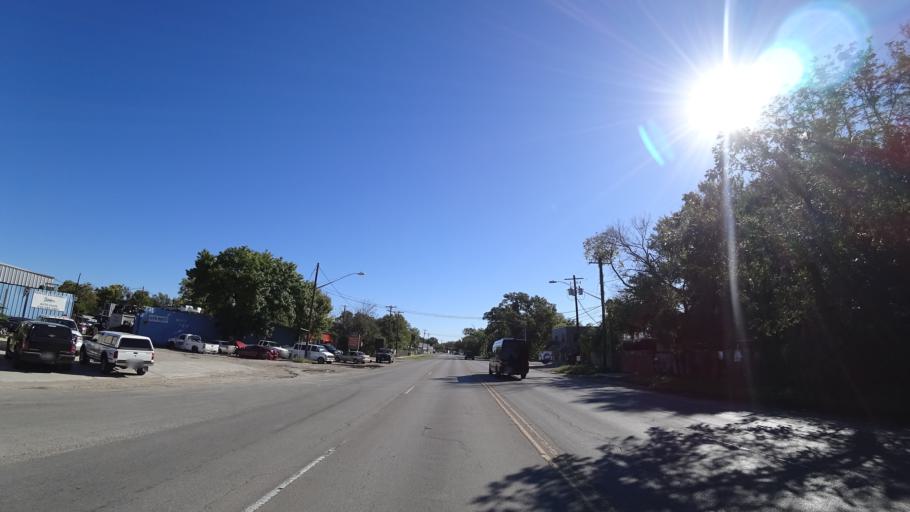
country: US
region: Texas
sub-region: Travis County
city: Austin
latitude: 30.2517
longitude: -97.7080
